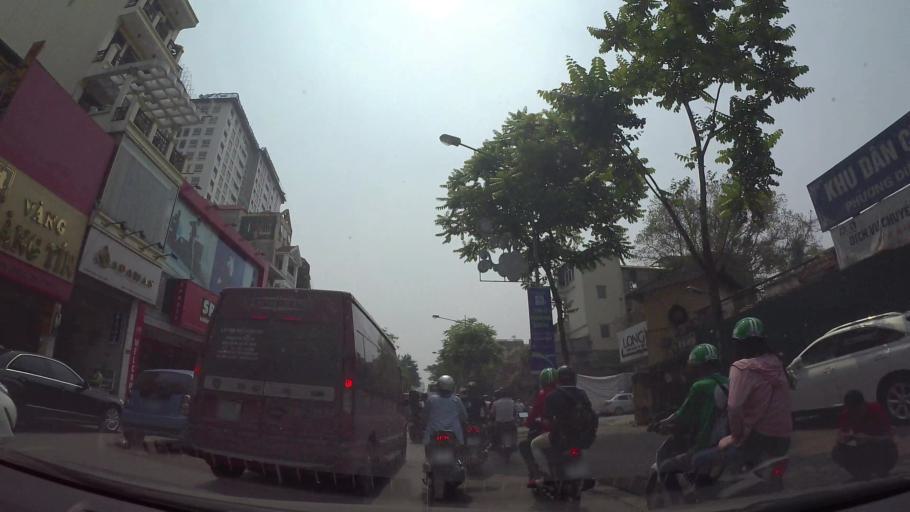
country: VN
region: Ha Noi
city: Dong Da
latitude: 21.0319
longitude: 105.8311
